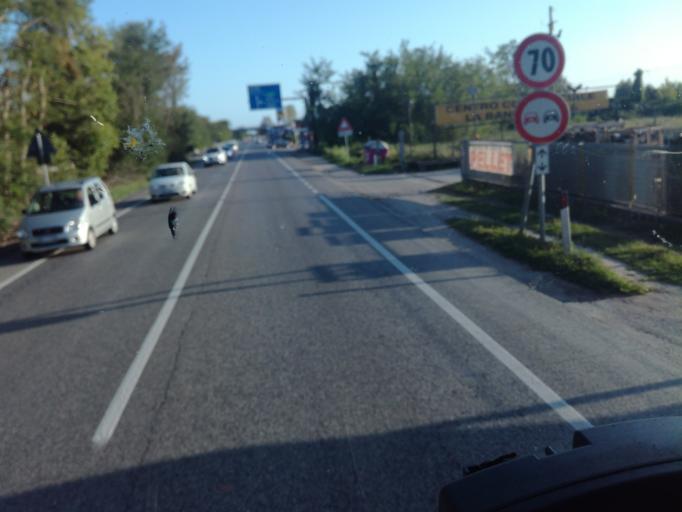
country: IT
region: Emilia-Romagna
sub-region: Provincia di Ferrara
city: Porto Garibaldi
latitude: 44.6922
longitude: 12.2229
